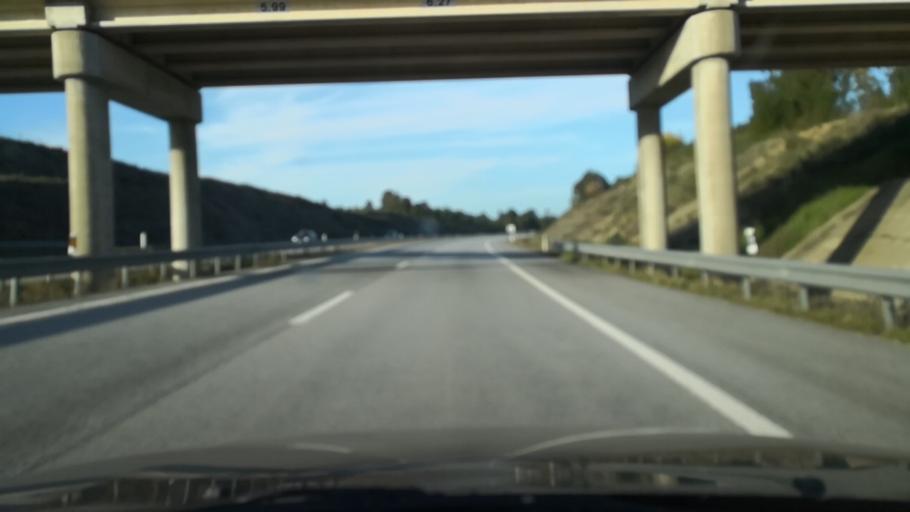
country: ES
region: Extremadura
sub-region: Provincia de Caceres
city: Cedillo
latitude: 39.7180
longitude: -7.6893
